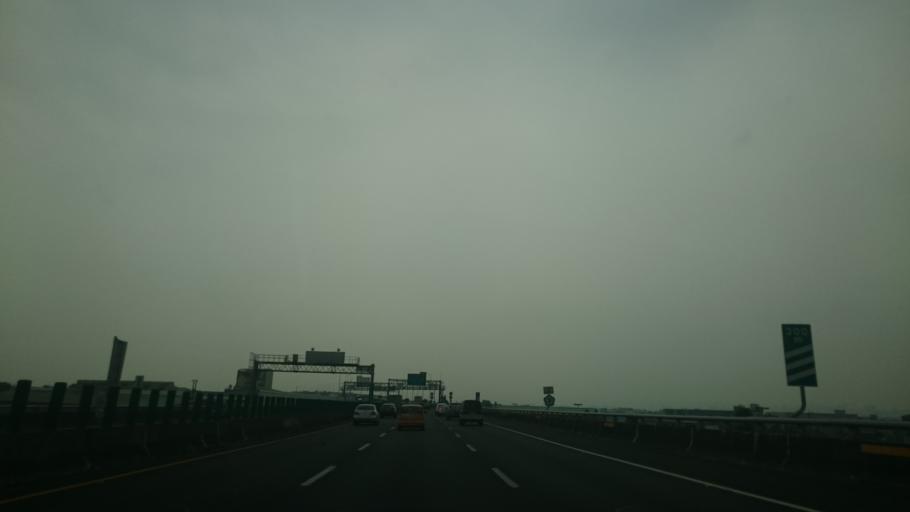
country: TW
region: Taiwan
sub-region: Taichung City
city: Taichung
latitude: 24.0591
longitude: 120.6731
